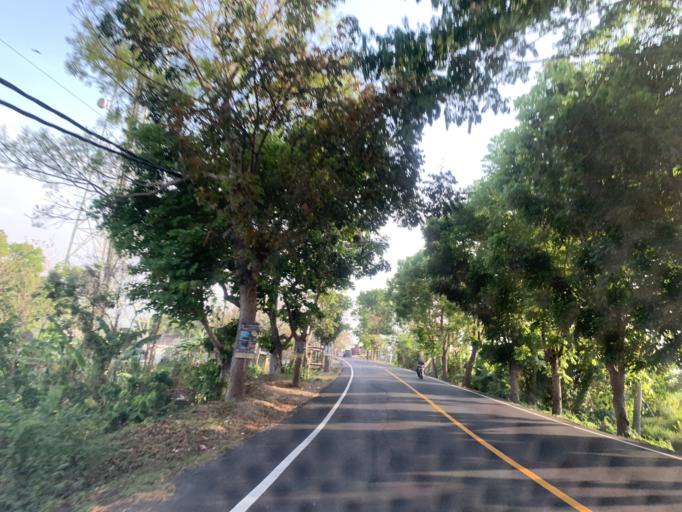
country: ID
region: Bali
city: Banjar Delodrurung
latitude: -8.5033
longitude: 115.0183
